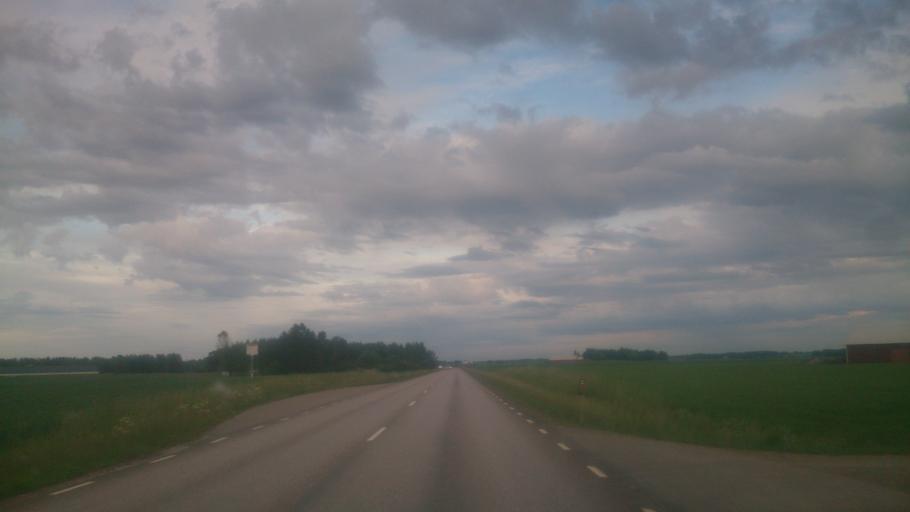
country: SE
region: OEstergoetland
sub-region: Motala Kommun
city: Borensberg
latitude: 58.4910
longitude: 15.3580
